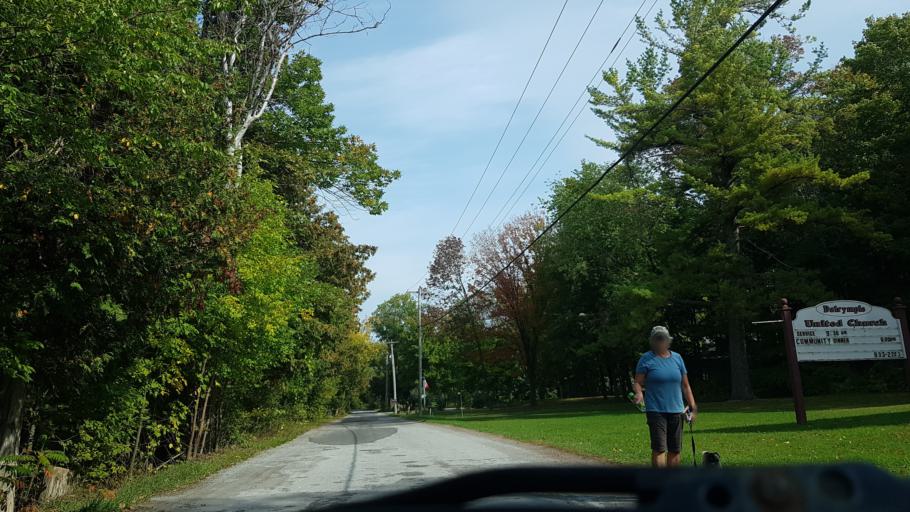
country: CA
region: Ontario
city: Orillia
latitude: 44.6624
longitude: -79.0995
